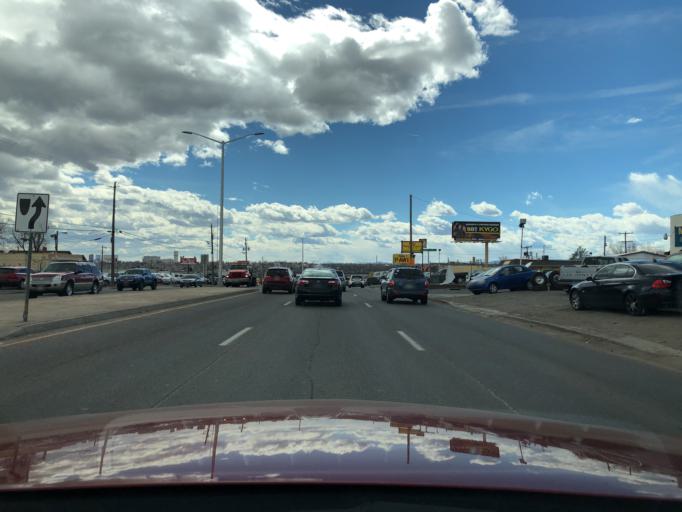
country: US
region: Colorado
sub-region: Adams County
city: Berkley
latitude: 39.8161
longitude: -105.0253
